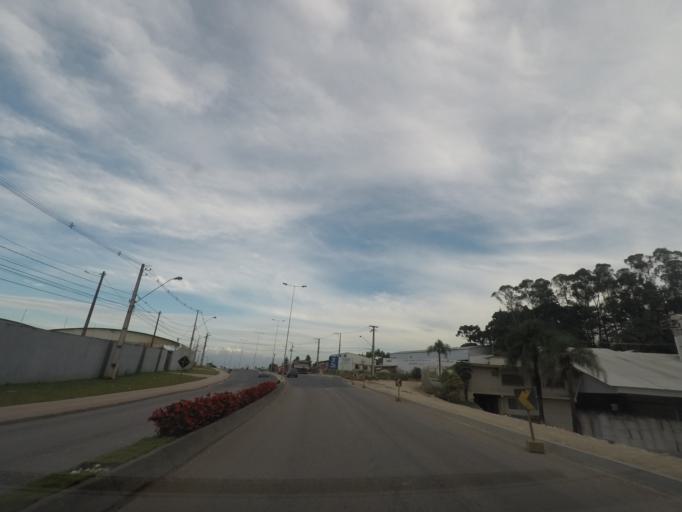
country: BR
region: Parana
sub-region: Colombo
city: Colombo
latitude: -25.2969
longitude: -49.2240
